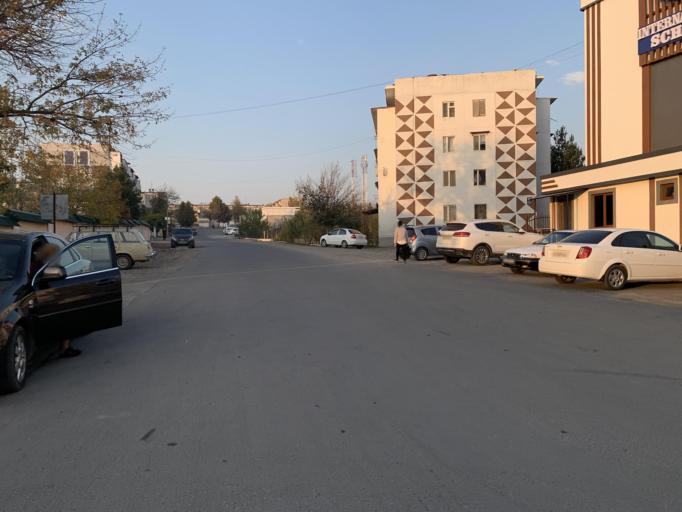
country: UZ
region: Namangan
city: Namangan Shahri
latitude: 41.0029
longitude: 71.5989
